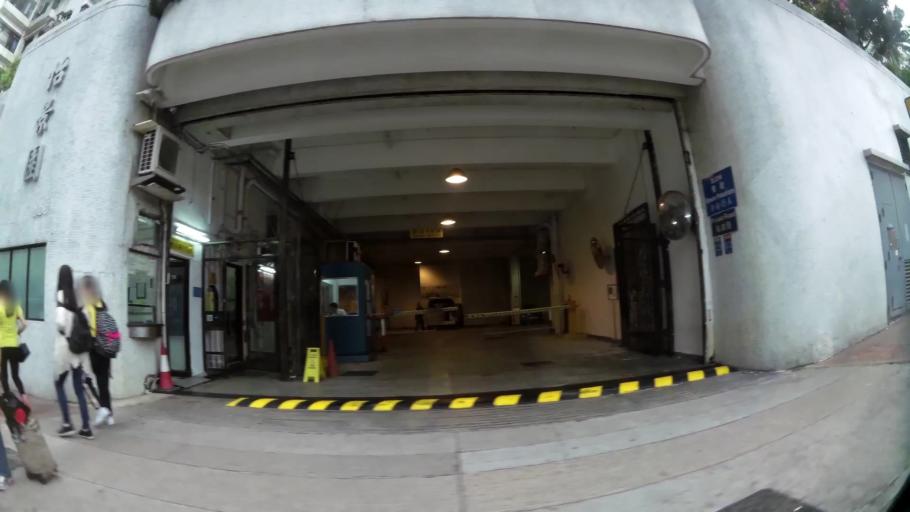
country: HK
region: Tsuen Wan
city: Tsuen Wan
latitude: 22.3739
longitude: 114.1213
